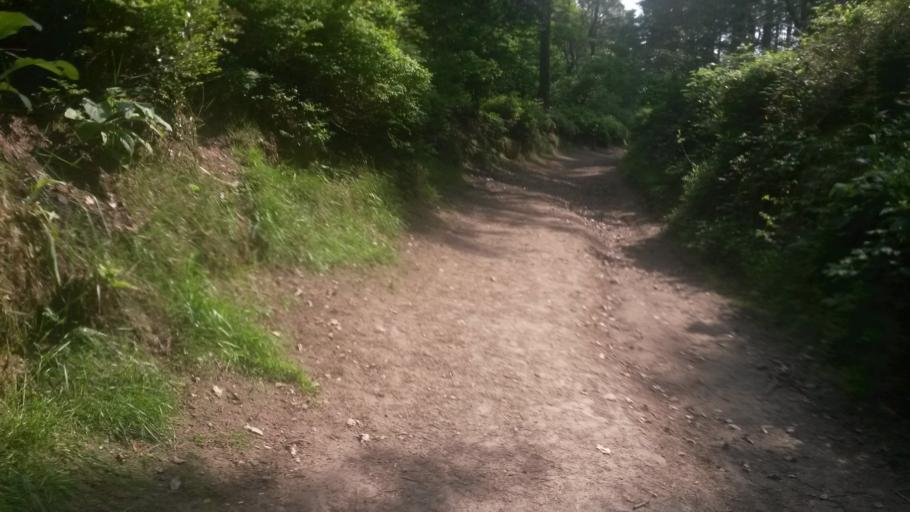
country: GB
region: England
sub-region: Surrey
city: Haslemere
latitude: 51.0667
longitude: -0.6870
